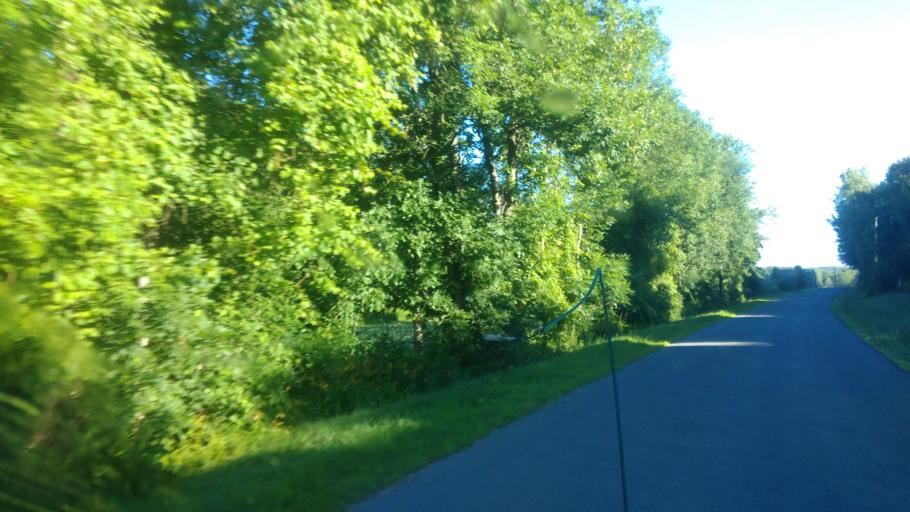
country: US
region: New York
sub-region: Wayne County
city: Lyons
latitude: 43.1393
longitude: -77.0421
